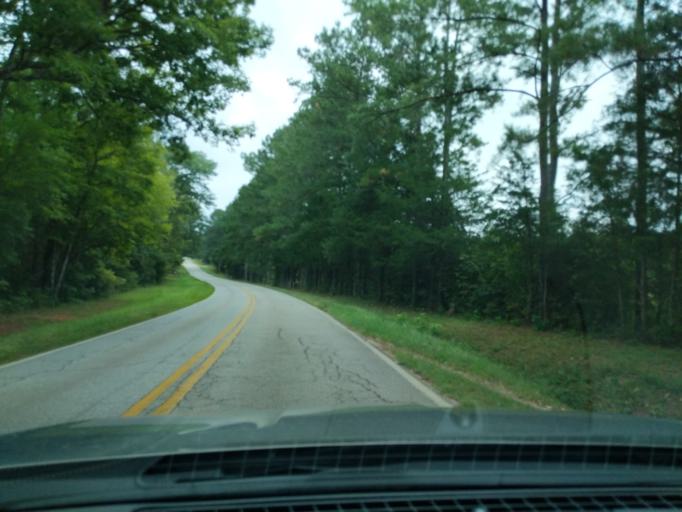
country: US
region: Georgia
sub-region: Columbia County
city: Appling
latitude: 33.5649
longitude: -82.3637
